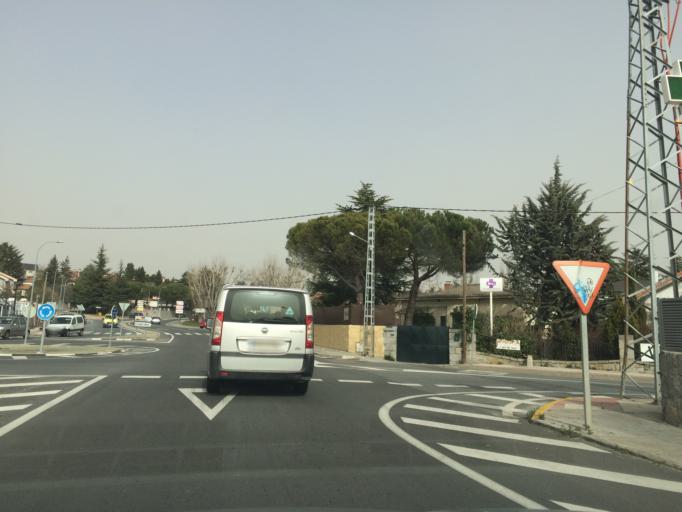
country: ES
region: Madrid
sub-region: Provincia de Madrid
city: Moralzarzal
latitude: 40.6744
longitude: -3.9701
